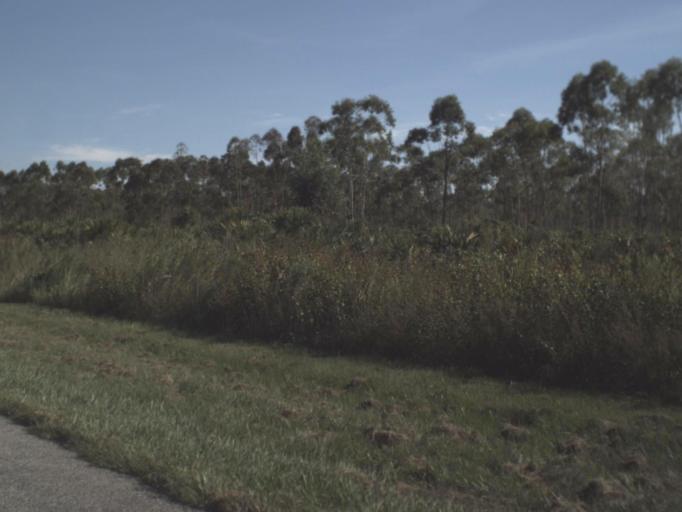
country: US
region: Florida
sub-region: Glades County
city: Moore Haven
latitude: 26.9088
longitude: -81.2701
